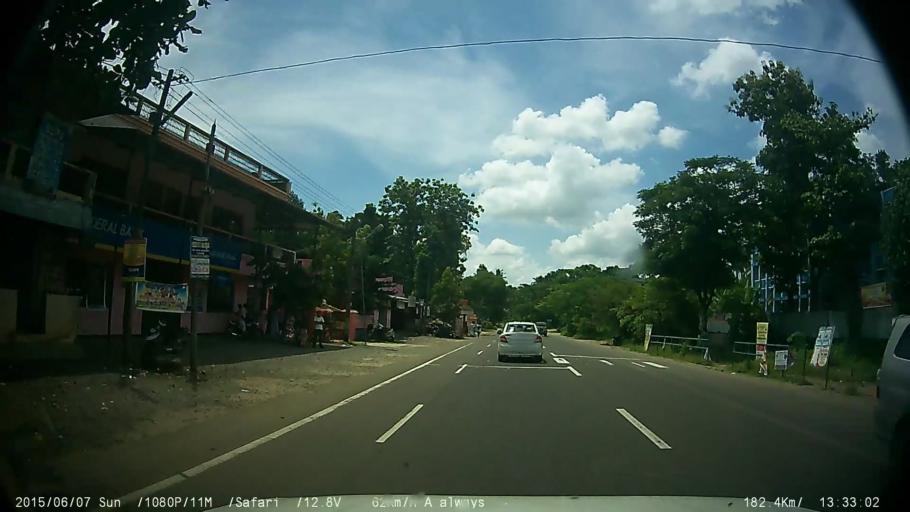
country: IN
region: Kerala
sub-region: Ernakulam
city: Perumbavoor
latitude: 10.0530
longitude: 76.5308
